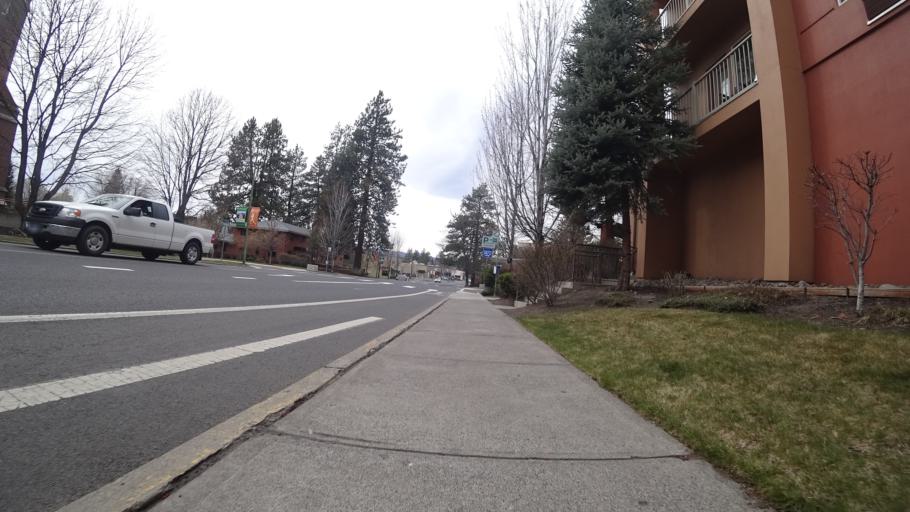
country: US
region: Oregon
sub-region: Deschutes County
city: Bend
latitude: 44.0564
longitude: -121.3114
